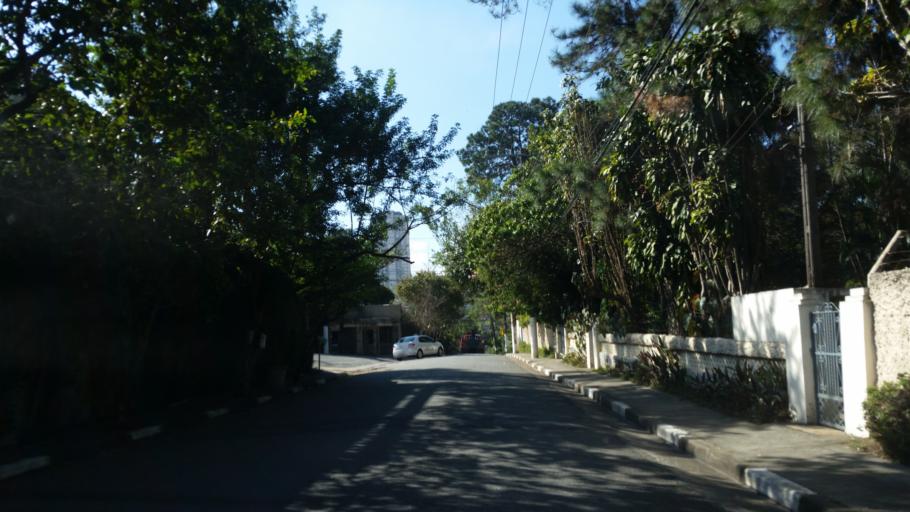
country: BR
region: Sao Paulo
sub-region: Diadema
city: Diadema
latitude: -23.6449
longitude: -46.6756
